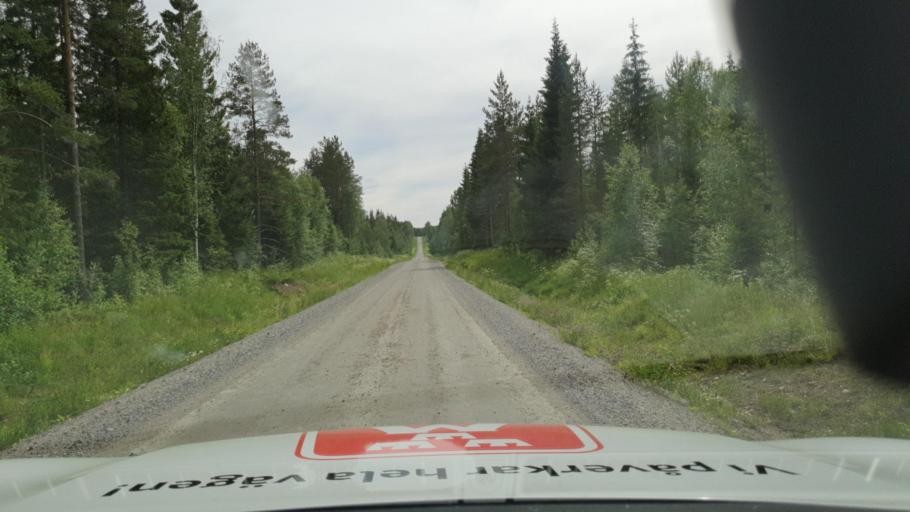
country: SE
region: Vaesterbotten
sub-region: Skelleftea Kommun
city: Burea
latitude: 64.4517
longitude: 21.0264
